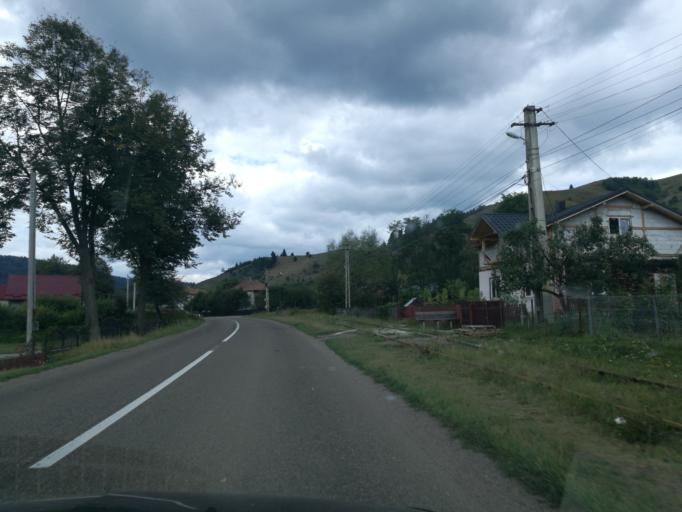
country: RO
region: Suceava
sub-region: Comuna Frumosu
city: Frumosu
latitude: 47.6164
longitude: 25.6368
